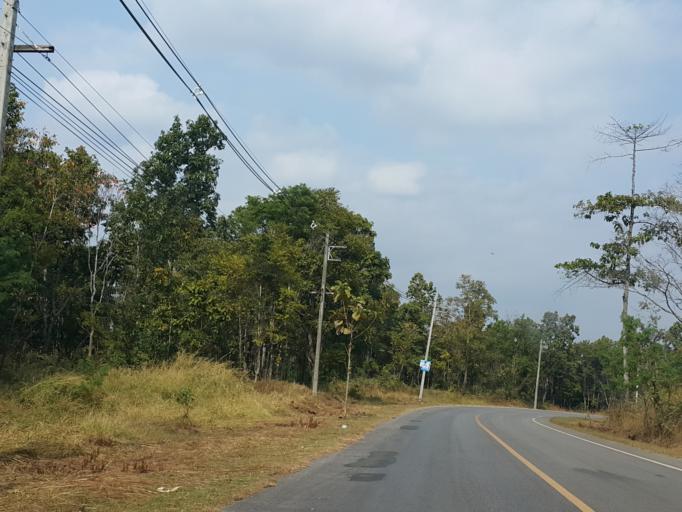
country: TH
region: Chiang Mai
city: Mae On
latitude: 18.8388
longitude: 99.2624
